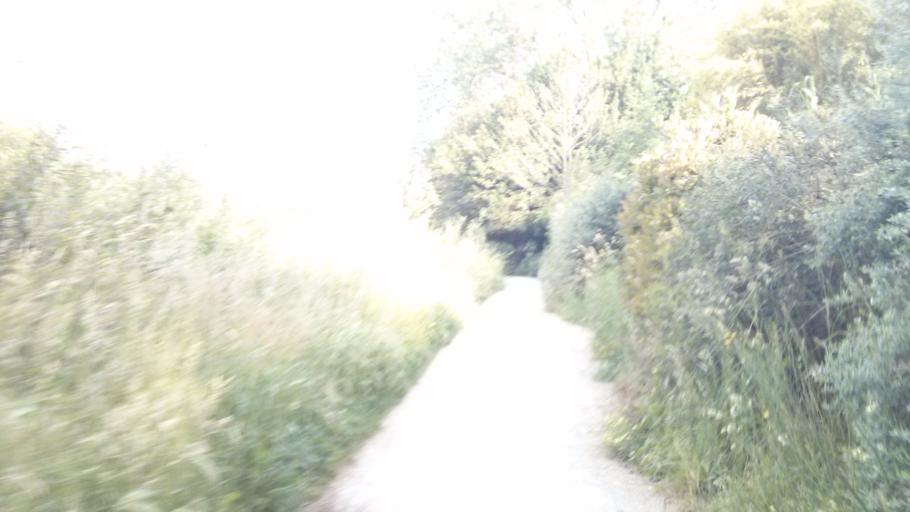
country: FR
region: Pays de la Loire
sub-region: Departement de la Loire-Atlantique
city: Reze
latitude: 47.1920
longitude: -1.5386
